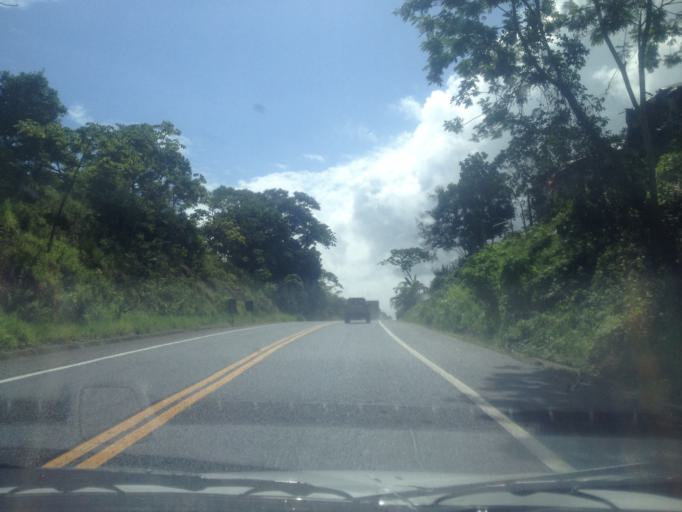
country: BR
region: Sergipe
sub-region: Indiaroba
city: Indiaroba
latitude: -11.6126
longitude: -37.5381
